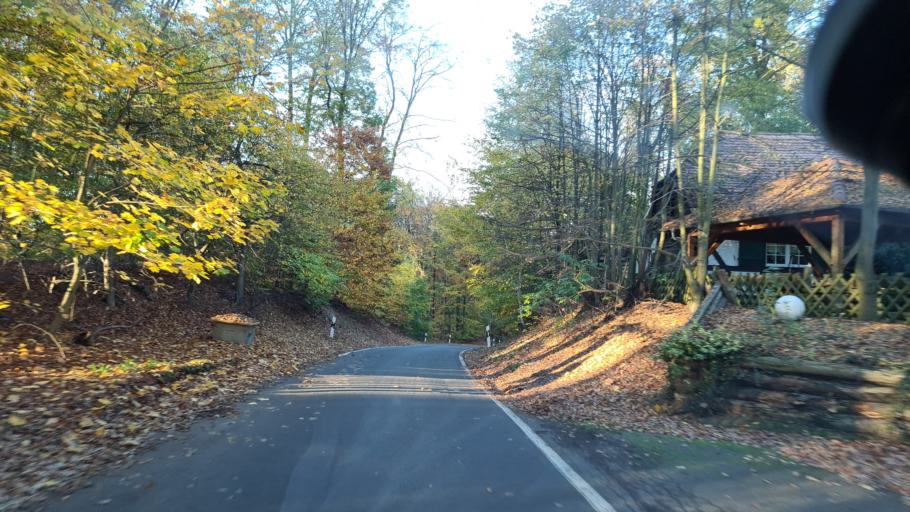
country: DE
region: Saxony
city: Dahlen
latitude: 51.4089
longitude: 13.0296
